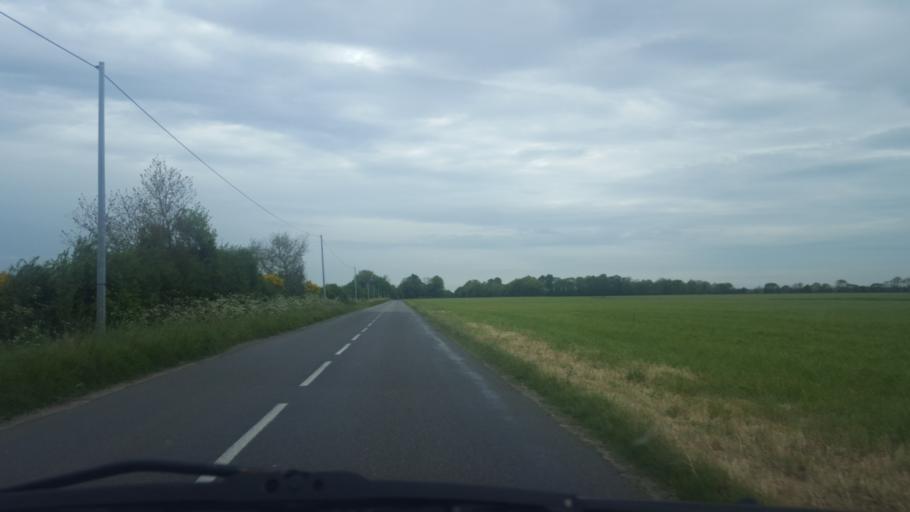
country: FR
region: Pays de la Loire
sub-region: Departement de la Loire-Atlantique
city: Geneston
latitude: 47.0425
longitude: -1.5209
